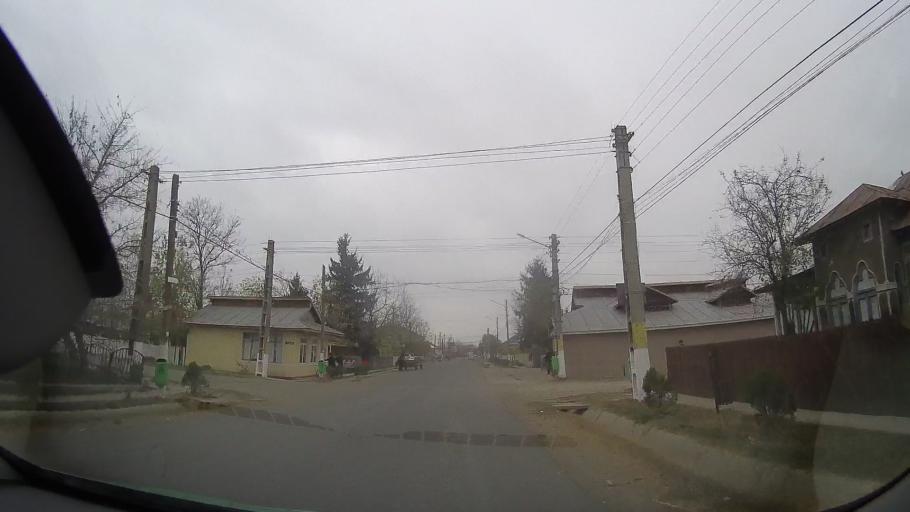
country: RO
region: Braila
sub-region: Comuna Ciocile
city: Ciocile
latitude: 44.8217
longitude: 27.2483
